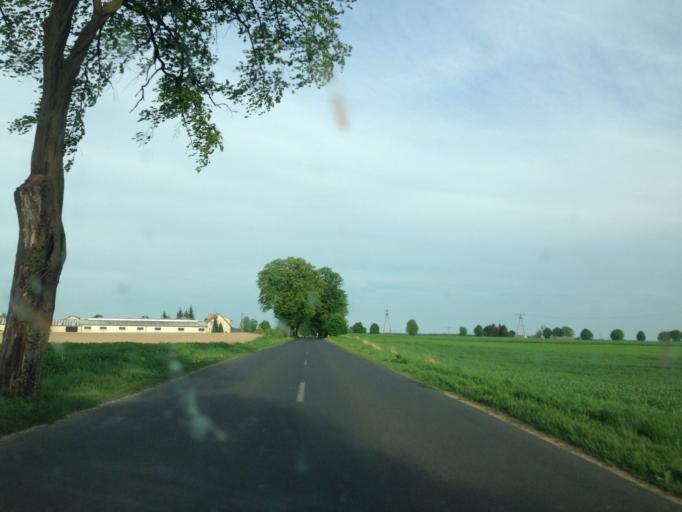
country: PL
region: Kujawsko-Pomorskie
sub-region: Powiat wabrzeski
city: Pluznica
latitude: 53.2870
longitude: 18.8578
